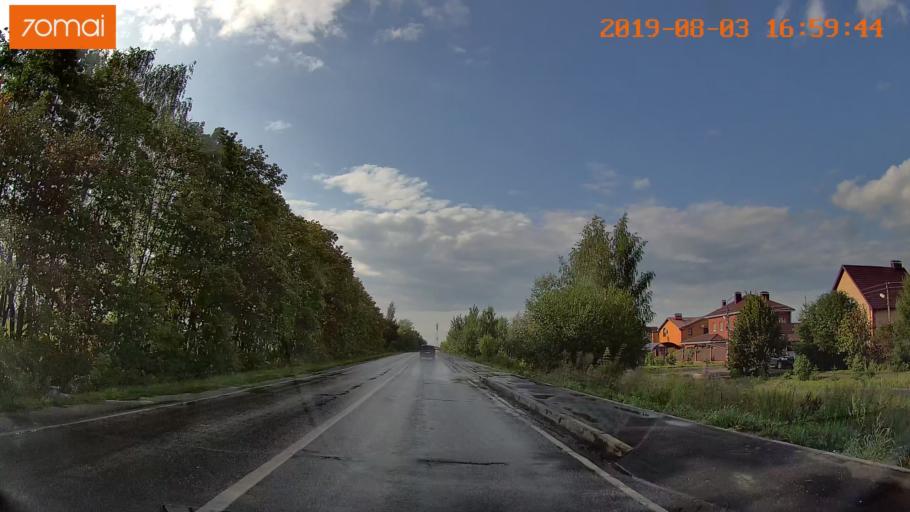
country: RU
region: Moskovskaya
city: Voskresensk
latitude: 55.3319
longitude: 38.6222
